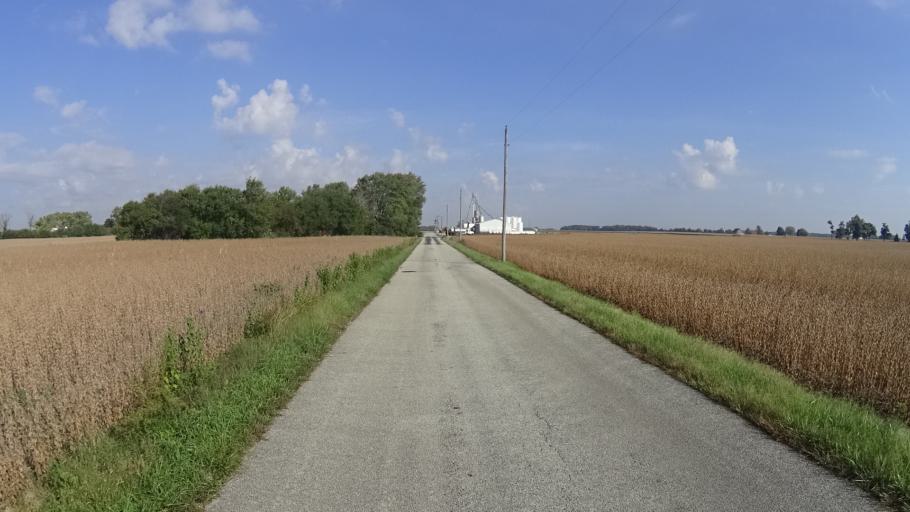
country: US
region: Indiana
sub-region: Madison County
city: Lapel
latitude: 40.0417
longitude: -85.8243
